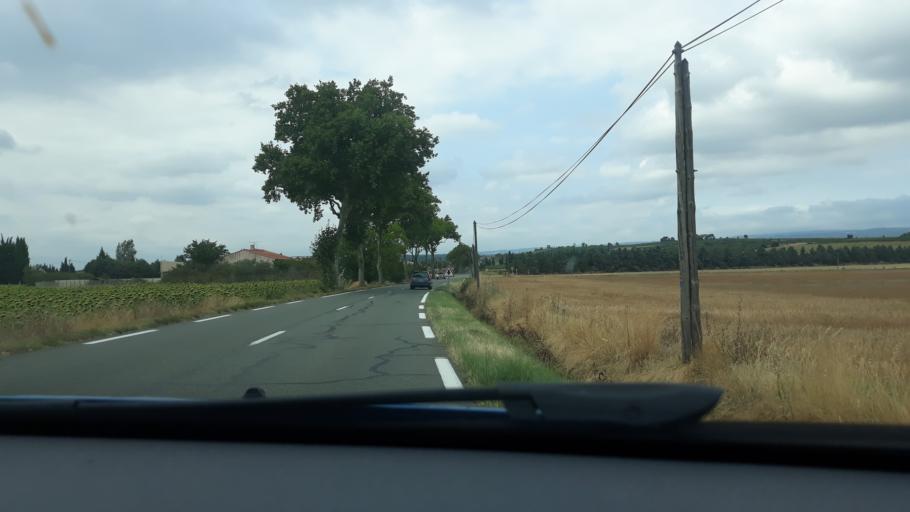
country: FR
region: Languedoc-Roussillon
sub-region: Departement de l'Aude
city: Pezens
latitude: 43.2630
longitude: 2.2443
